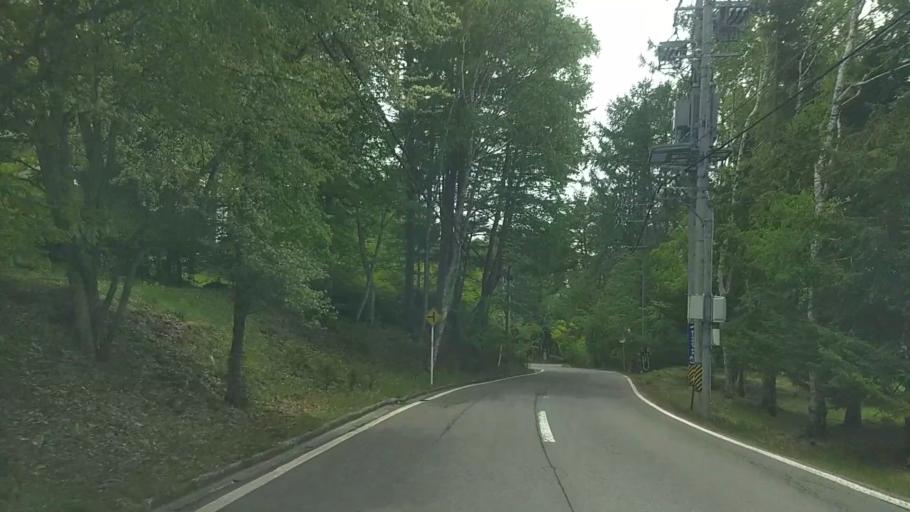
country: JP
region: Nagano
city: Chino
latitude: 36.0460
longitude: 138.2695
